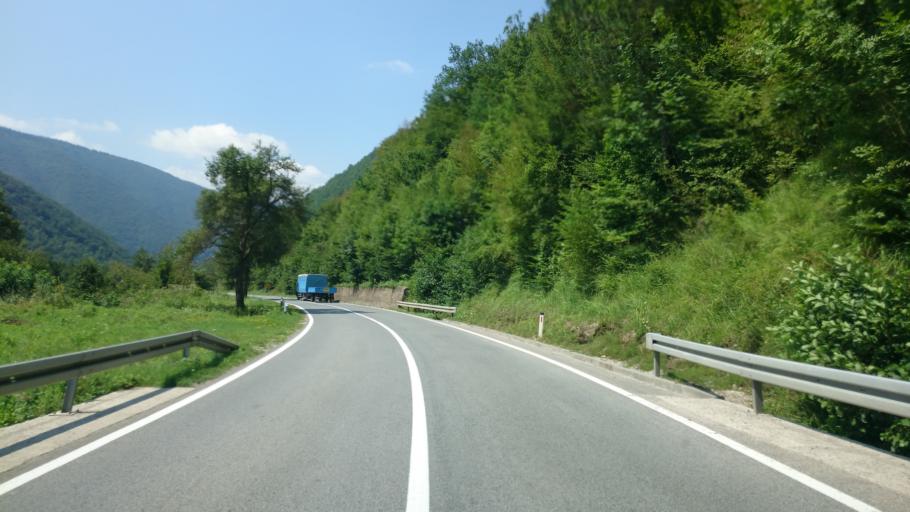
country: BA
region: Federation of Bosnia and Herzegovina
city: Donji Vakuf
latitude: 44.2045
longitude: 17.3432
